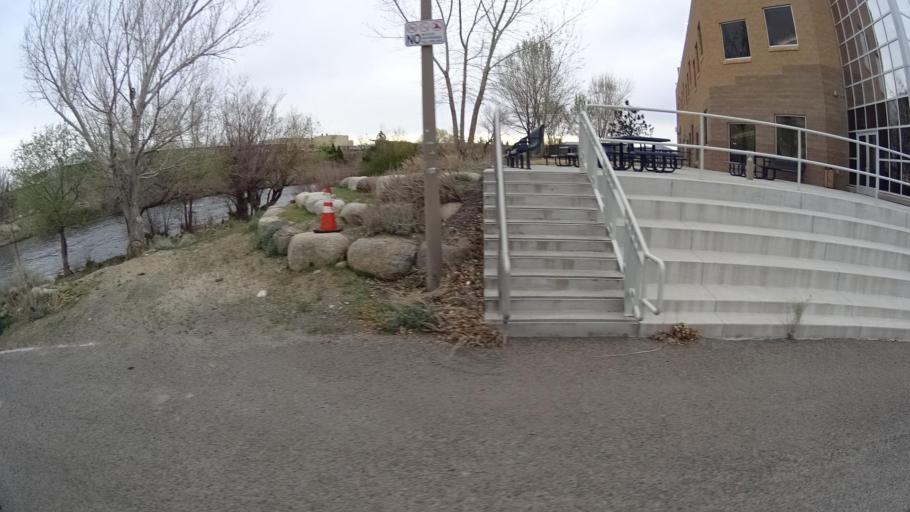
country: US
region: Nevada
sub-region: Washoe County
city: Reno
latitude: 39.5303
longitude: -119.7918
